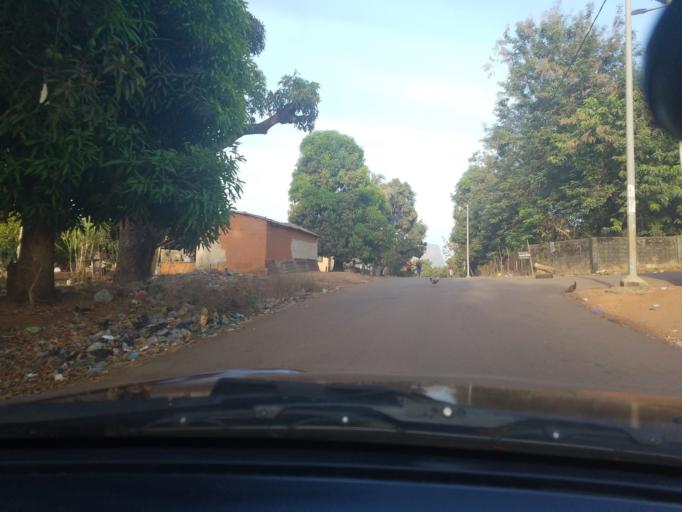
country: GN
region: Kindia
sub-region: Prefecture de Dubreka
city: Dubreka
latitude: 9.7883
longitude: -13.5166
